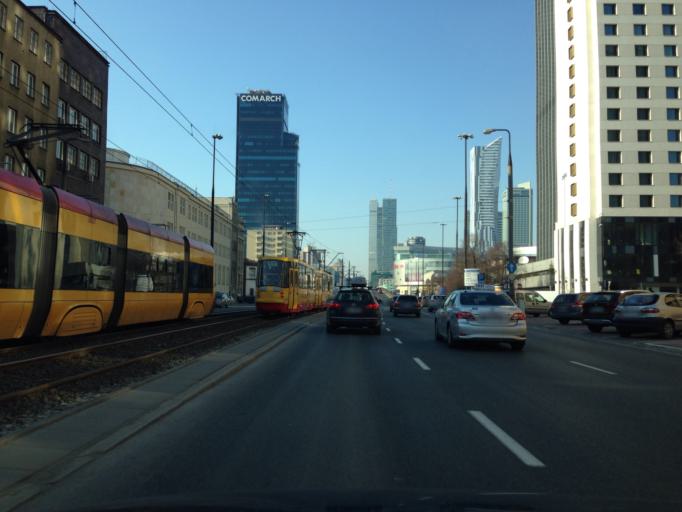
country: PL
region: Masovian Voivodeship
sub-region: Warszawa
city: Warsaw
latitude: 52.2244
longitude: 21.0040
